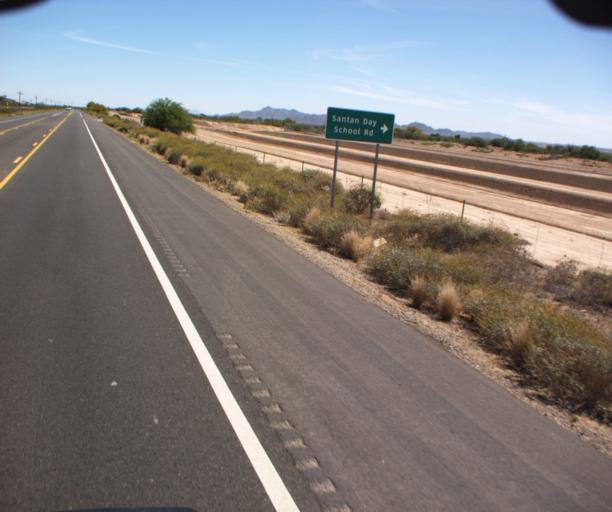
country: US
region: Arizona
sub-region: Pinal County
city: Sacaton
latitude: 33.1459
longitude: -111.7643
